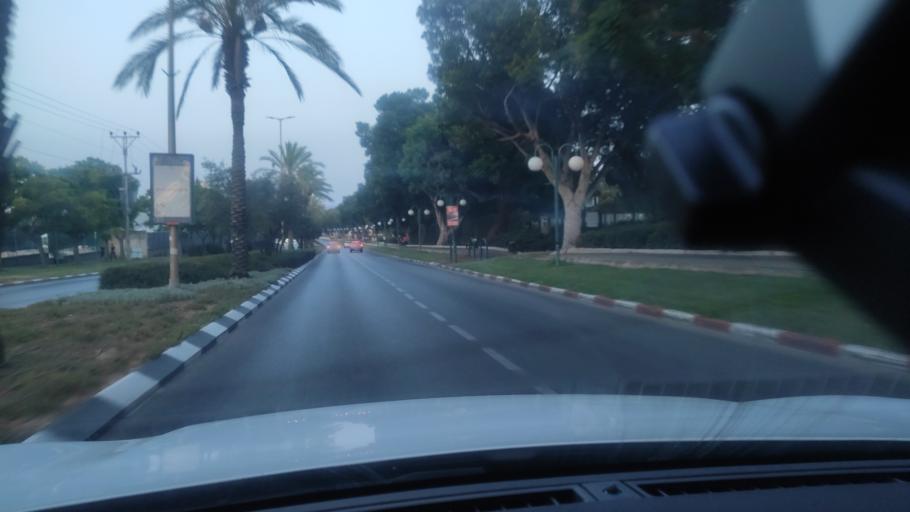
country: IL
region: Central District
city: Kfar Saba
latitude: 32.1830
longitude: 34.9241
